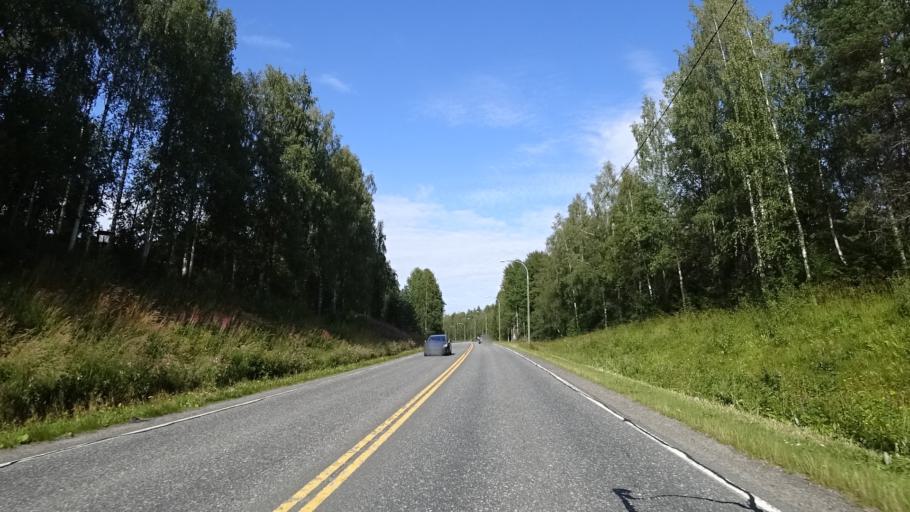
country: FI
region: North Karelia
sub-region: Joensuu
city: Eno
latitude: 62.7828
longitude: 30.0756
